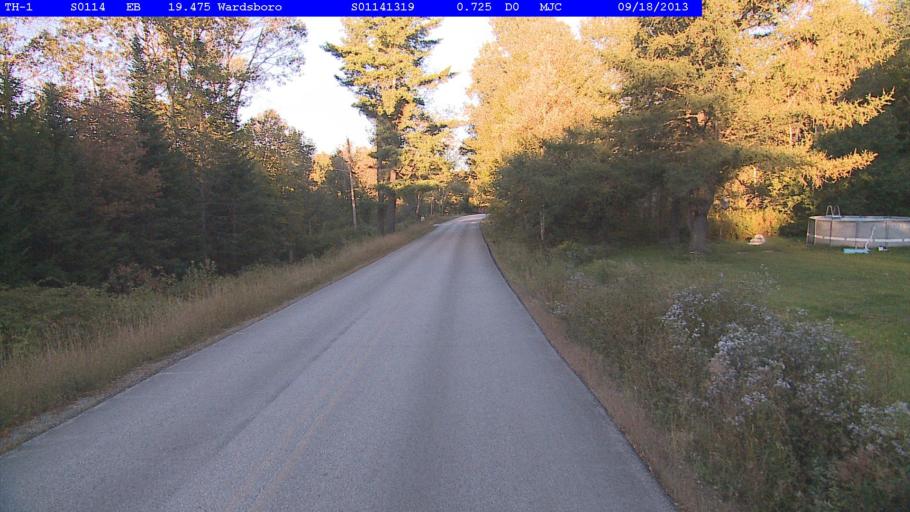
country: US
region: Vermont
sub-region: Windham County
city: Dover
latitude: 43.0289
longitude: -72.8619
